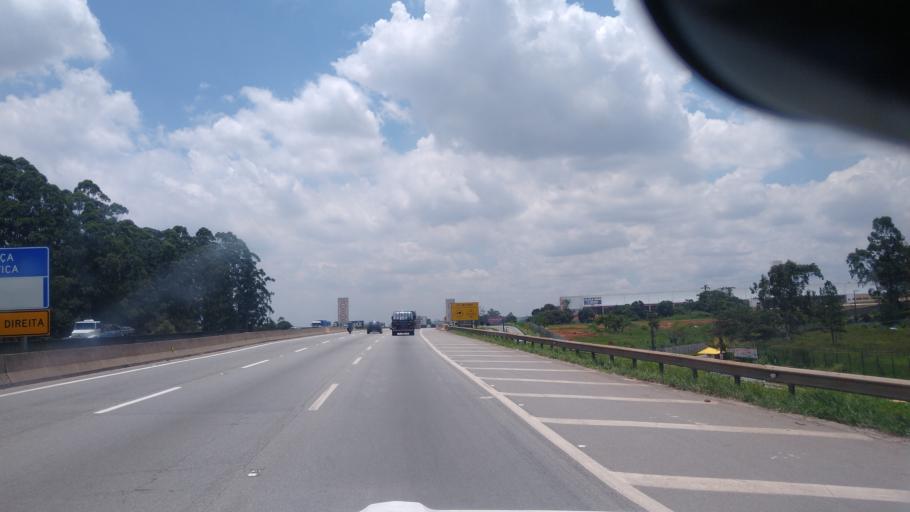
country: BR
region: Sao Paulo
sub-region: Itaquaquecetuba
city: Itaquaquecetuba
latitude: -23.4666
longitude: -46.3531
